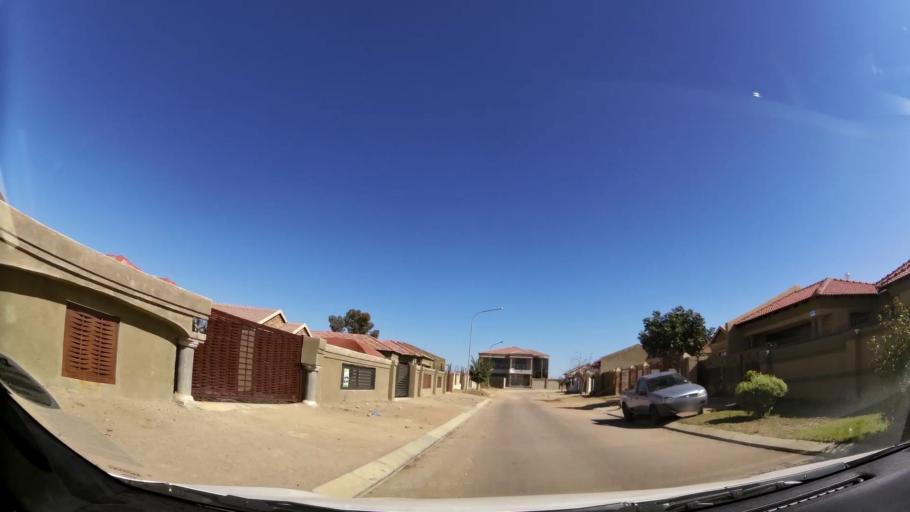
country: ZA
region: Limpopo
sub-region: Capricorn District Municipality
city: Polokwane
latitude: -23.8613
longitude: 29.4257
